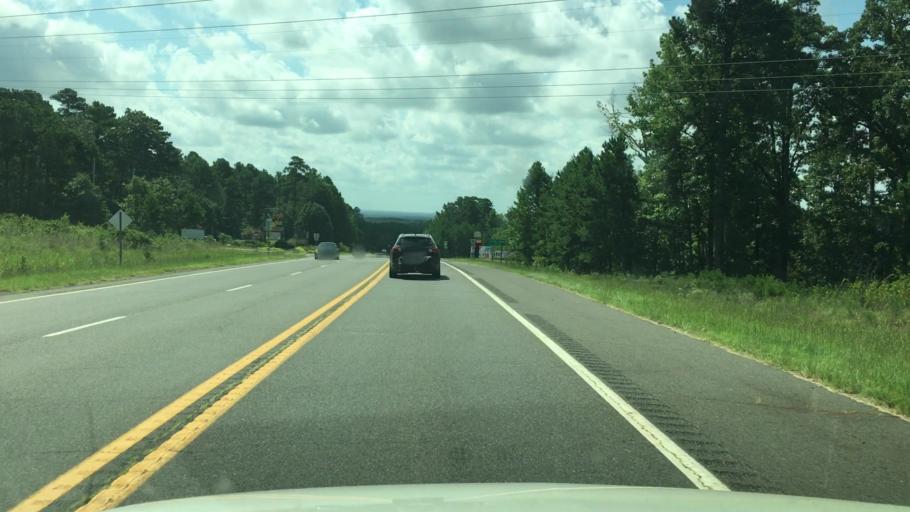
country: US
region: Arkansas
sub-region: Clark County
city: Arkadelphia
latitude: 34.2154
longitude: -93.0844
